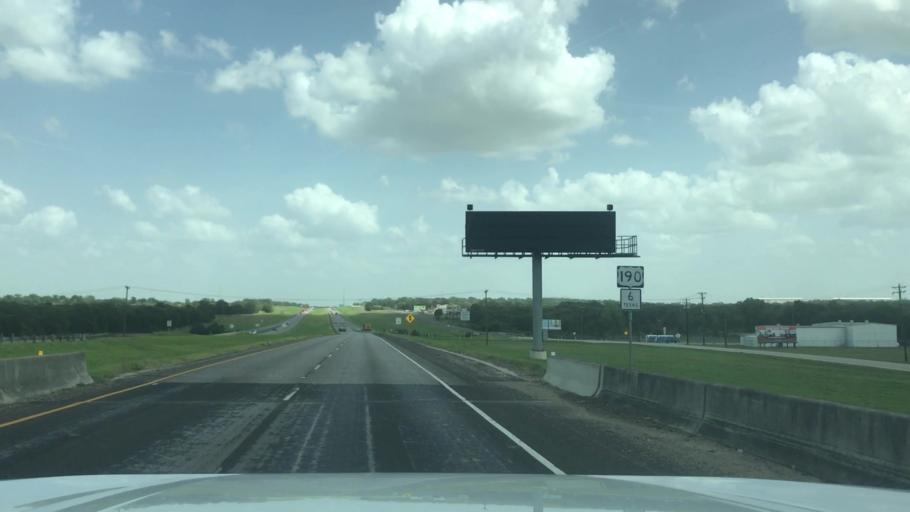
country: US
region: Texas
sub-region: Brazos County
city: Bryan
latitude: 30.7469
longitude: -96.4561
